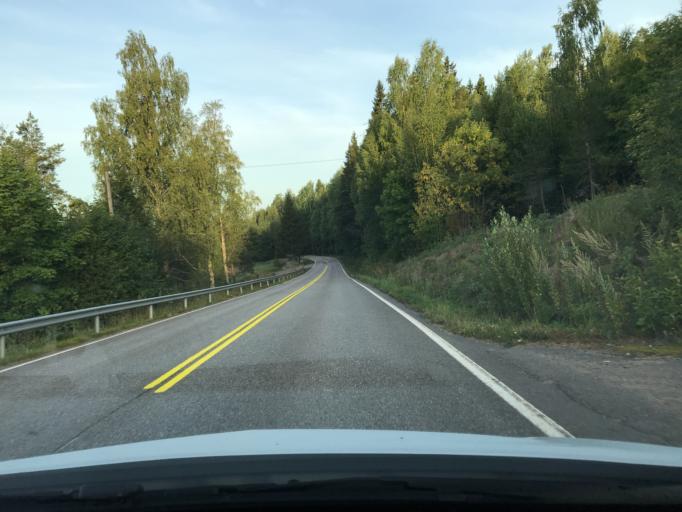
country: FI
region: Uusimaa
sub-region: Helsinki
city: Vihti
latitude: 60.4185
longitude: 24.4920
